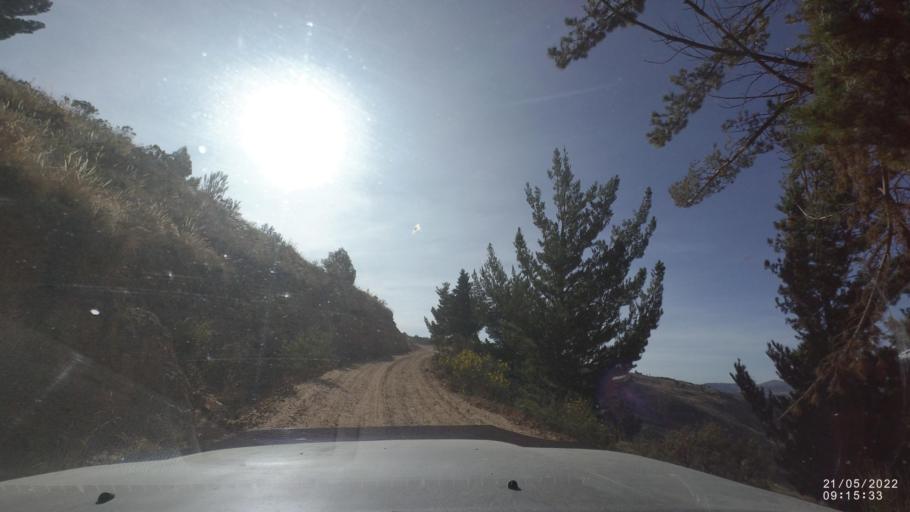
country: BO
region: Cochabamba
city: Cochabamba
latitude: -17.3647
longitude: -66.0271
